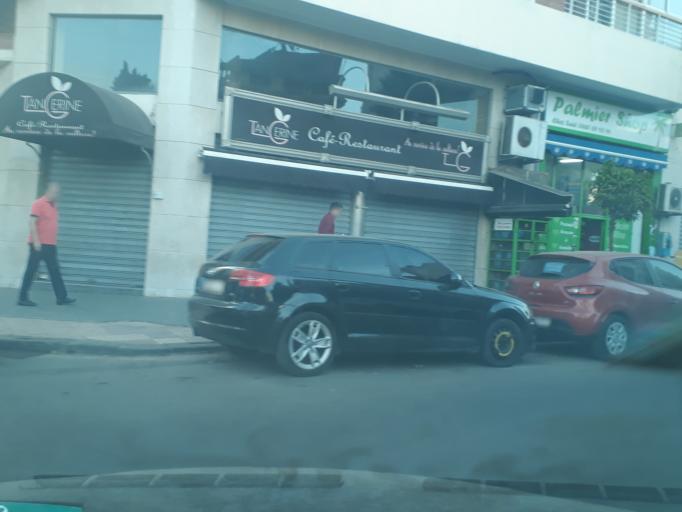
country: MA
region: Grand Casablanca
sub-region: Casablanca
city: Casablanca
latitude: 33.5794
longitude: -7.6265
